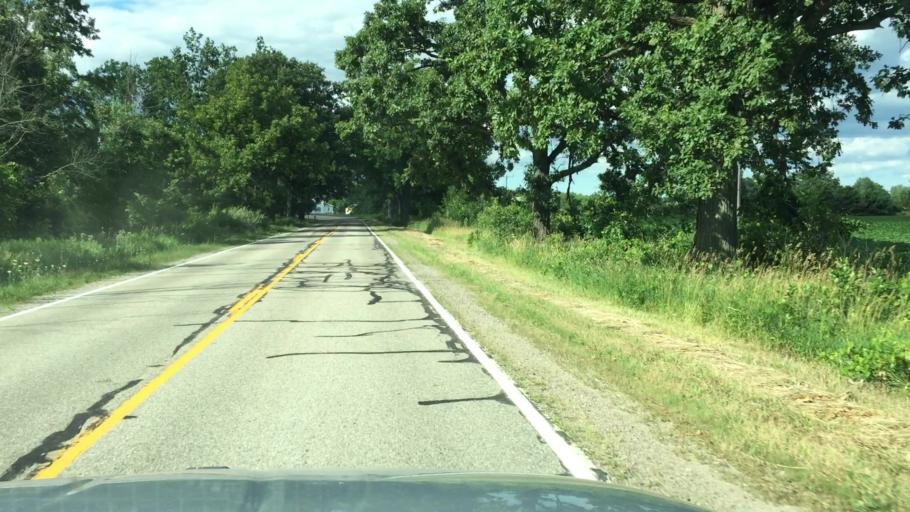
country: US
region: Michigan
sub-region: Saint Clair County
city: Capac
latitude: 43.0903
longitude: -82.9103
